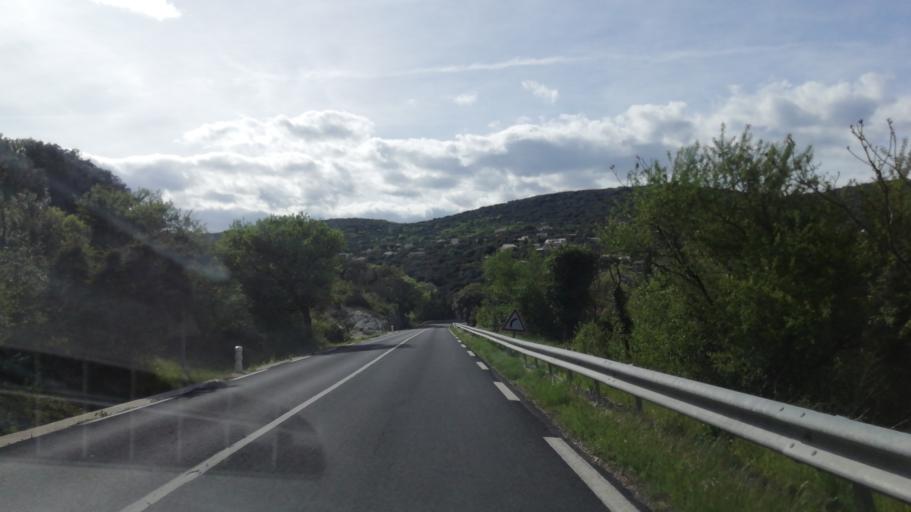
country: FR
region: Languedoc-Roussillon
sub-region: Departement de l'Herault
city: Saint-Martin-de-Londres
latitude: 43.7724
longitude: 3.7231
